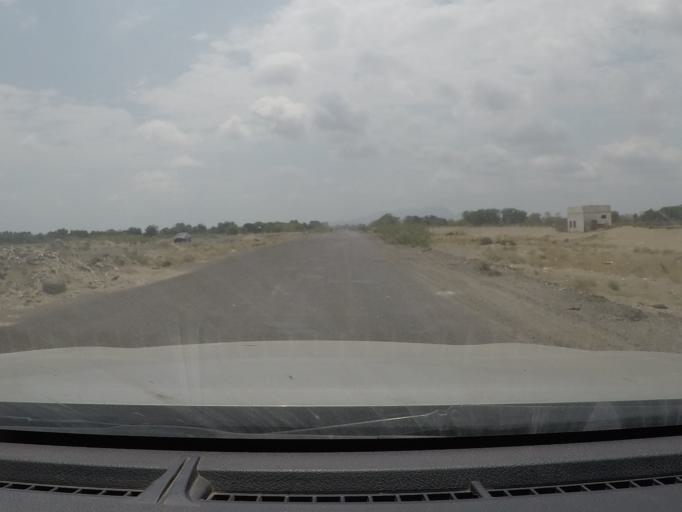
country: YE
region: Aden
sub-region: Ash Shaikh Outhman
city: Ash Shaykh `Uthman
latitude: 12.9185
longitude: 45.0085
